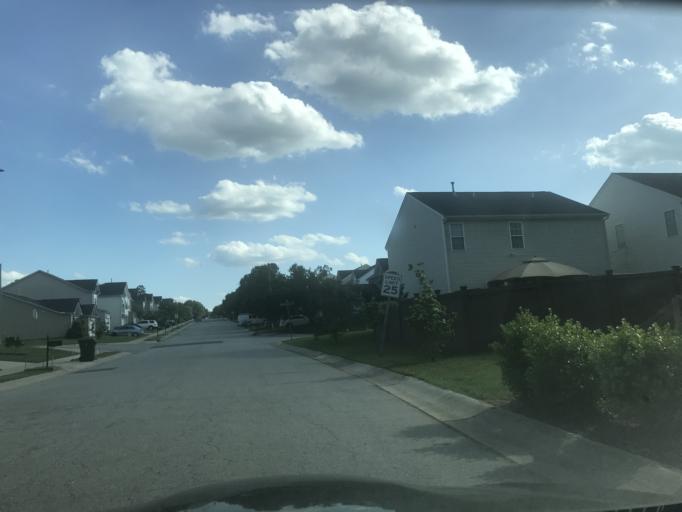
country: US
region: North Carolina
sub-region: Wake County
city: Knightdale
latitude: 35.8399
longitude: -78.5475
